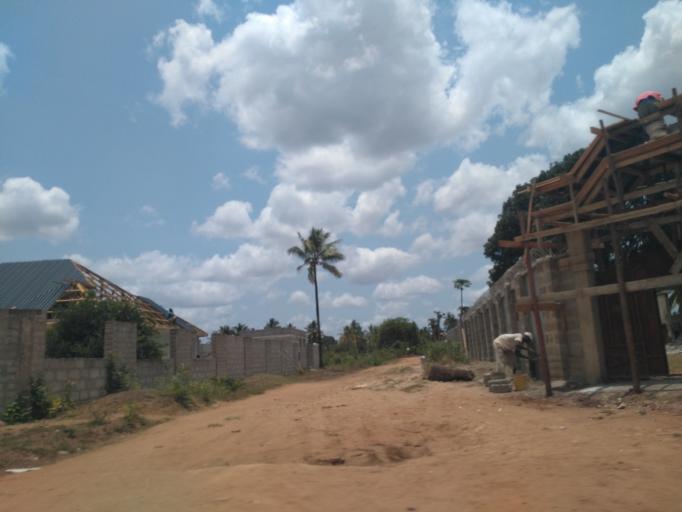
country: TZ
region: Dar es Salaam
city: Dar es Salaam
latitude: -6.8406
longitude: 39.3338
